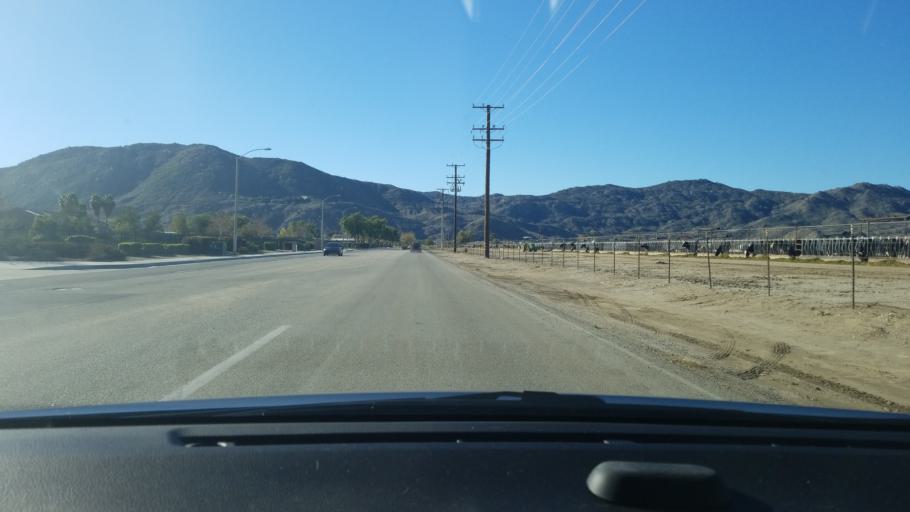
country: US
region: California
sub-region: Riverside County
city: San Jacinto
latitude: 33.7873
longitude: -117.0181
